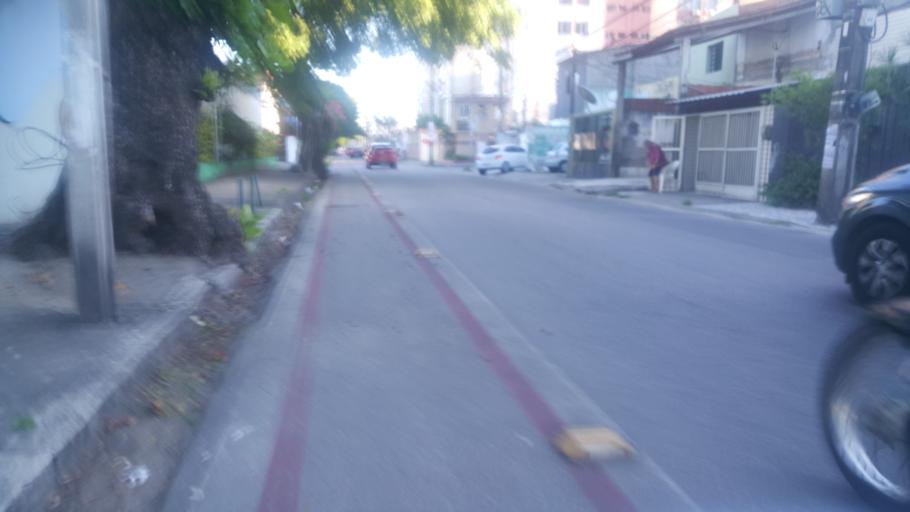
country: BR
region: Ceara
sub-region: Fortaleza
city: Fortaleza
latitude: -3.7397
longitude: -38.5334
